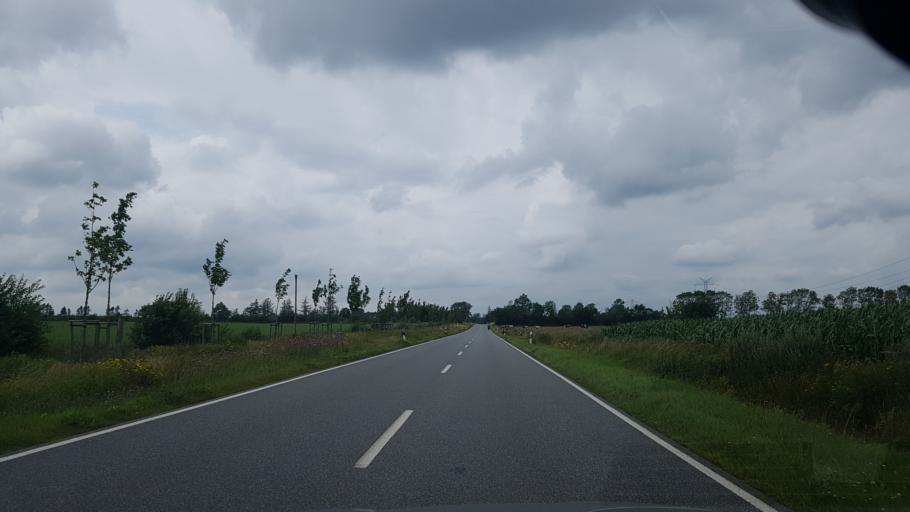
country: DE
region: Schleswig-Holstein
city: Osterby
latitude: 54.8124
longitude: 9.2316
